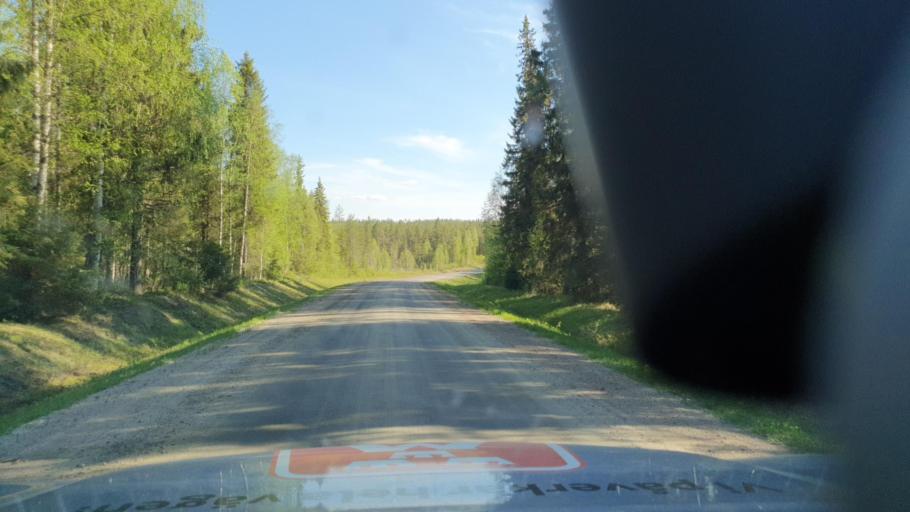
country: SE
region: Norrbotten
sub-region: Alvsbyns Kommun
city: AElvsbyn
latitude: 66.2909
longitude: 21.1550
